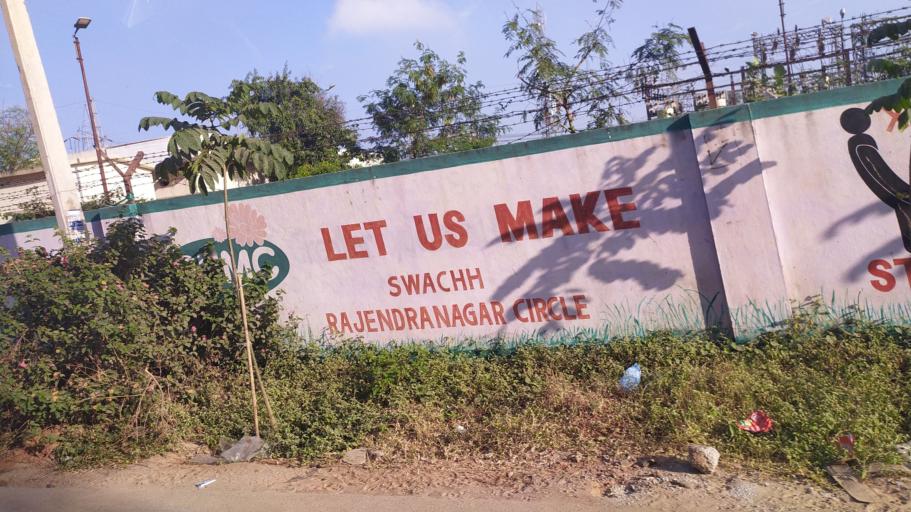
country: IN
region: Telangana
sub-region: Hyderabad
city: Hyderabad
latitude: 17.3269
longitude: 78.4242
